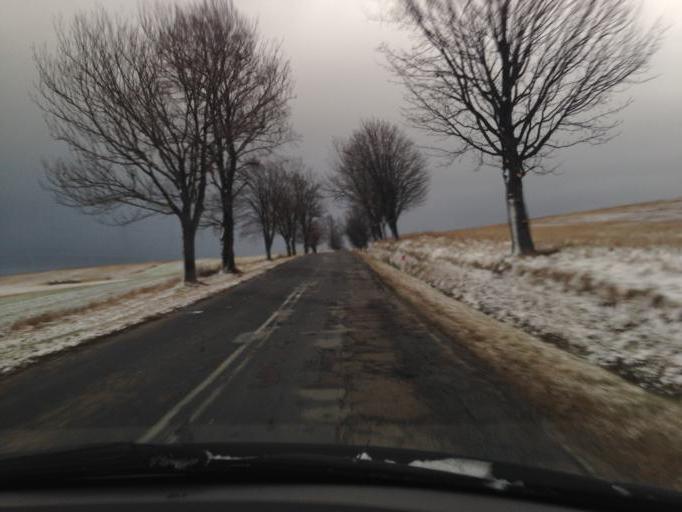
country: PL
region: Subcarpathian Voivodeship
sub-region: Powiat jasielski
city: Nowy Zmigrod
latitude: 49.6099
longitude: 21.5019
